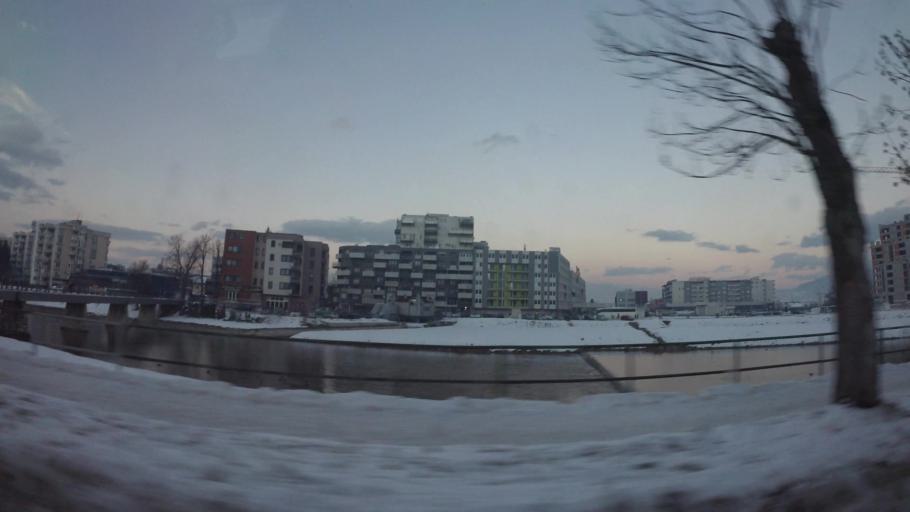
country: BA
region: Federation of Bosnia and Herzegovina
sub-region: Kanton Sarajevo
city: Sarajevo
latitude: 43.8279
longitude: 18.3072
